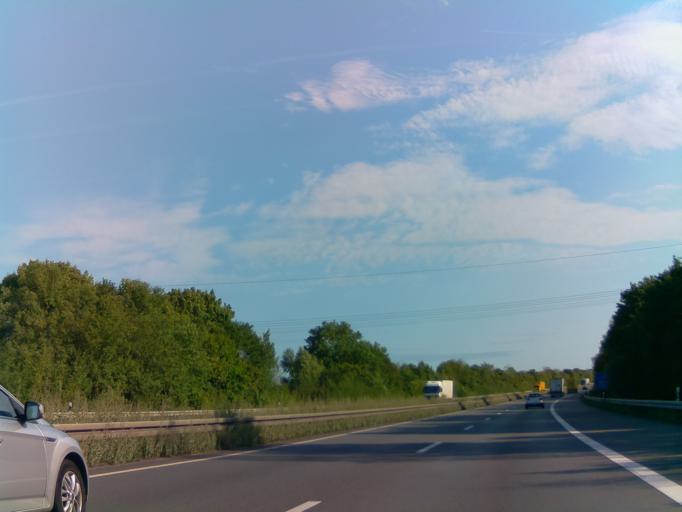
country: DE
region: Hesse
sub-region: Regierungsbezirk Darmstadt
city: Alsbach-Hahnlein
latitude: 49.7594
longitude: 8.5966
